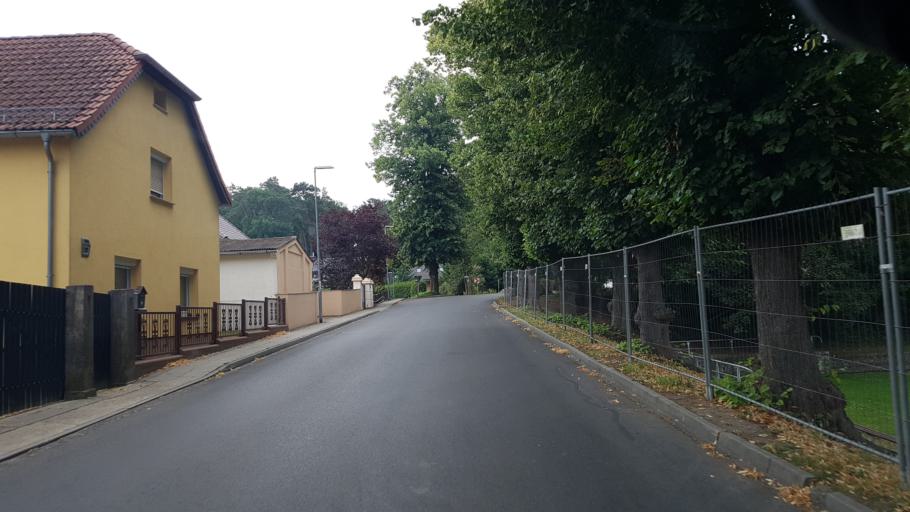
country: DE
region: Brandenburg
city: Hirschfeld
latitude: 51.3818
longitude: 13.6142
